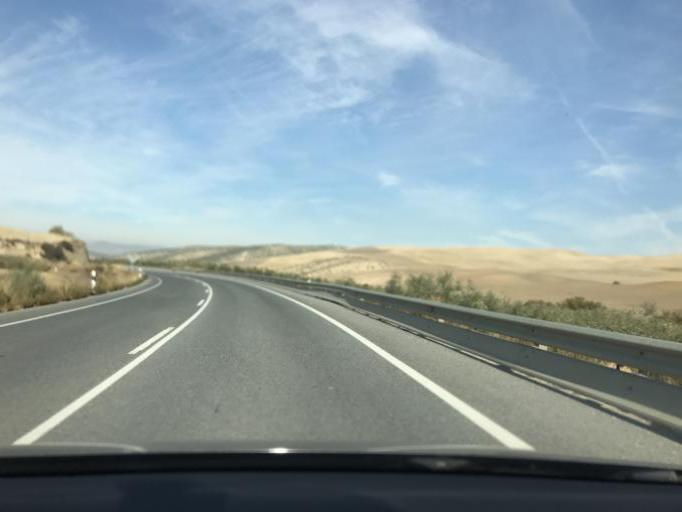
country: ES
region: Andalusia
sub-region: Provincia de Granada
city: Las Gabias
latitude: 37.1268
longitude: -3.7288
